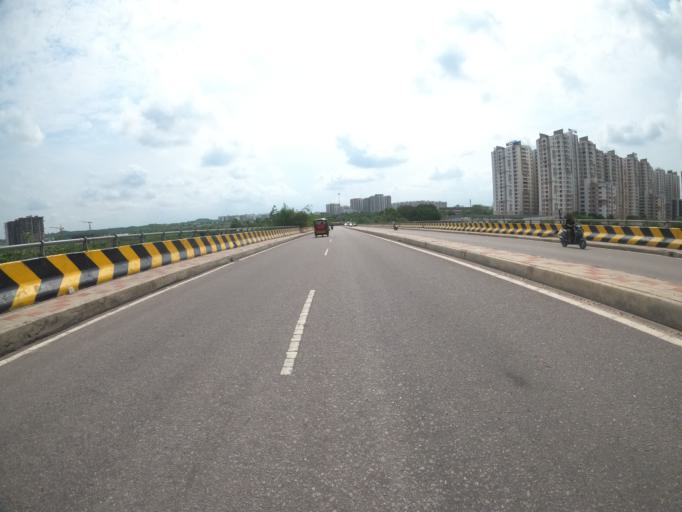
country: IN
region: Telangana
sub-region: Hyderabad
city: Hyderabad
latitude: 17.3862
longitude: 78.3502
